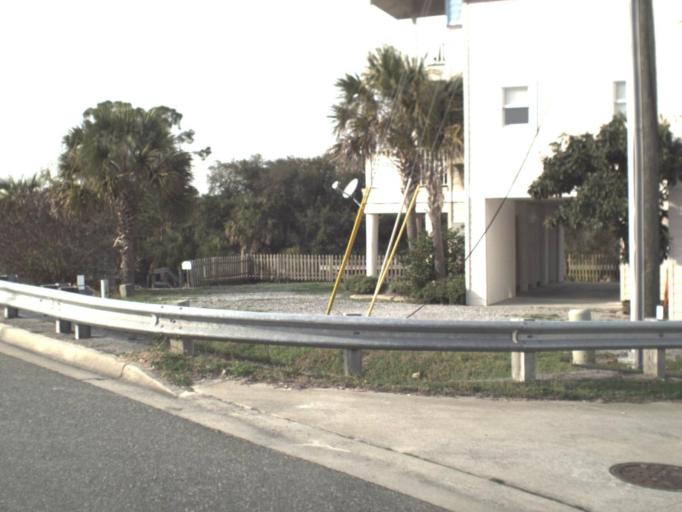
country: US
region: Florida
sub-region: Bay County
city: Mexico Beach
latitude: 29.9531
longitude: -85.4264
